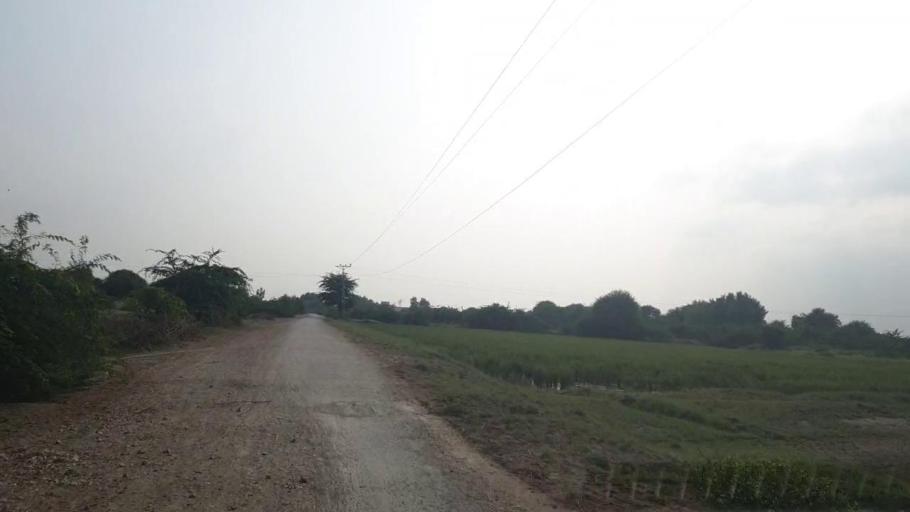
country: PK
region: Sindh
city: Badin
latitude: 24.6148
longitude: 68.6862
